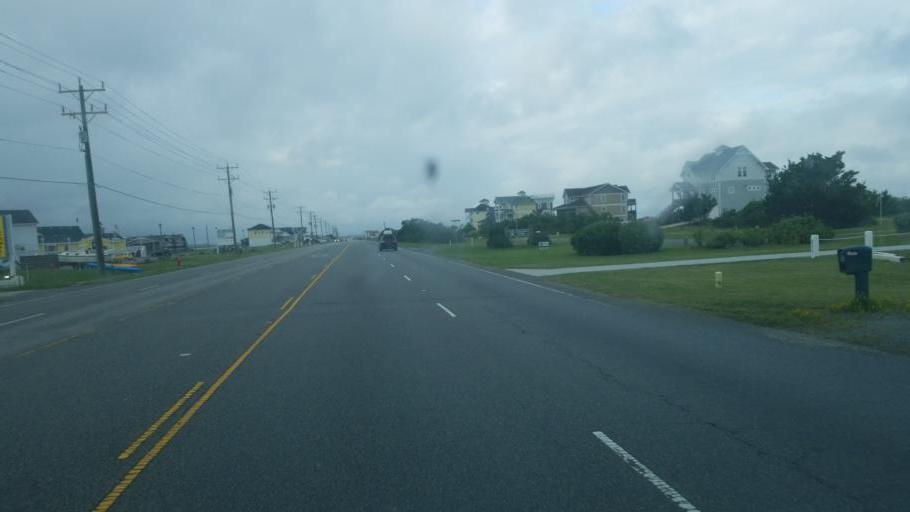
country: US
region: North Carolina
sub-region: Dare County
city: Nags Head
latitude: 35.9029
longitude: -75.6061
